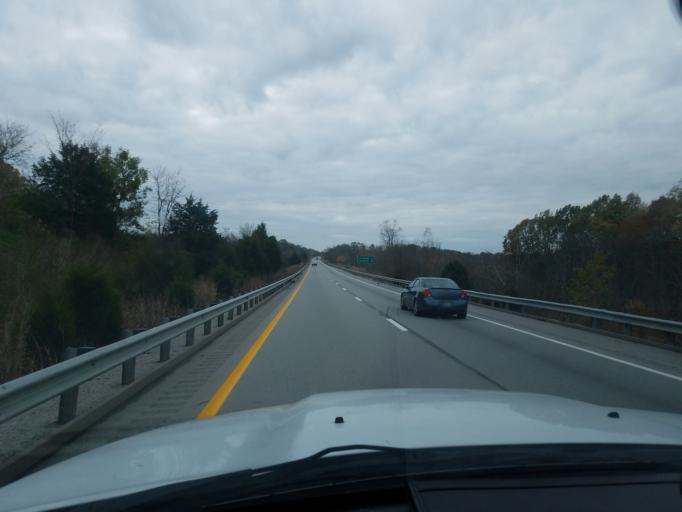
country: US
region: Kentucky
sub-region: Trimble County
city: Providence
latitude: 38.5101
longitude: -85.2418
